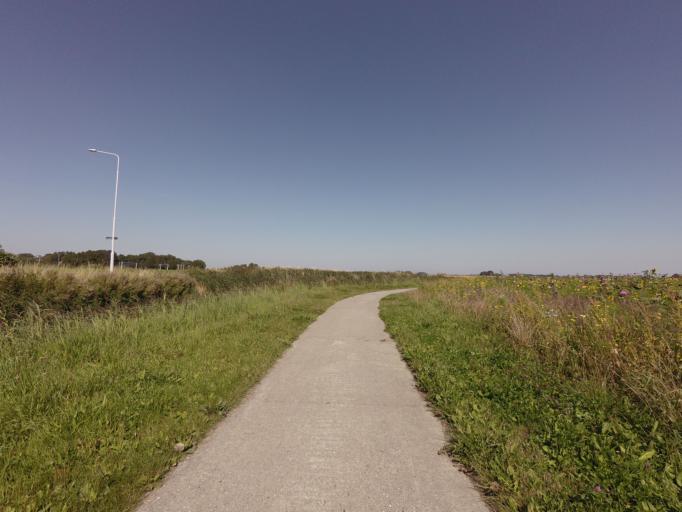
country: NL
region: Friesland
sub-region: Gemeente Dongeradeel
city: Anjum
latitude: 53.3837
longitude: 6.0564
